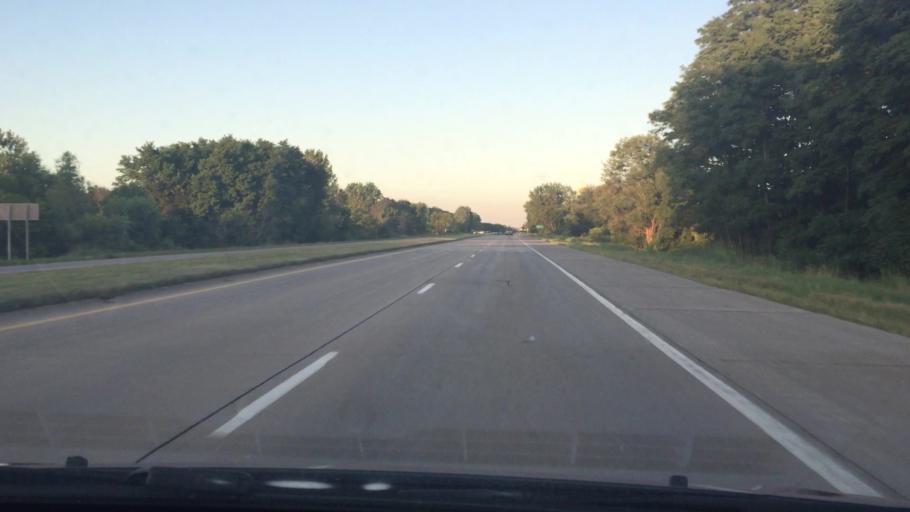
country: US
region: Iowa
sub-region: Muscatine County
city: Muscatine
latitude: 41.4525
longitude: -91.0683
